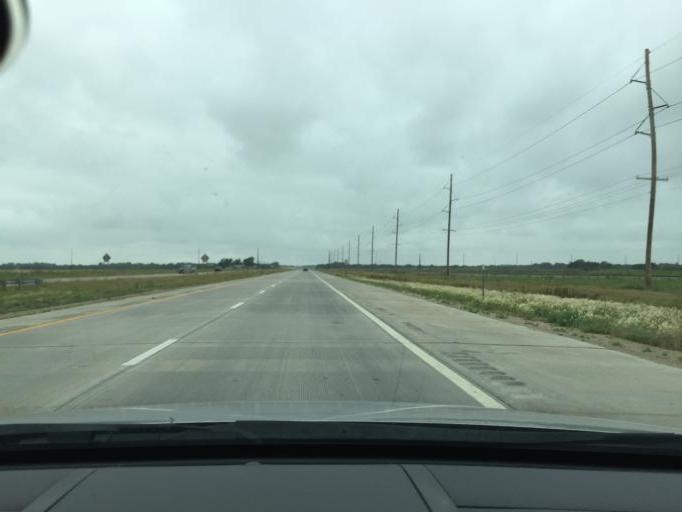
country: US
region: Kansas
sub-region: Reno County
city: Hutchinson
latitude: 38.0290
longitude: -97.8761
